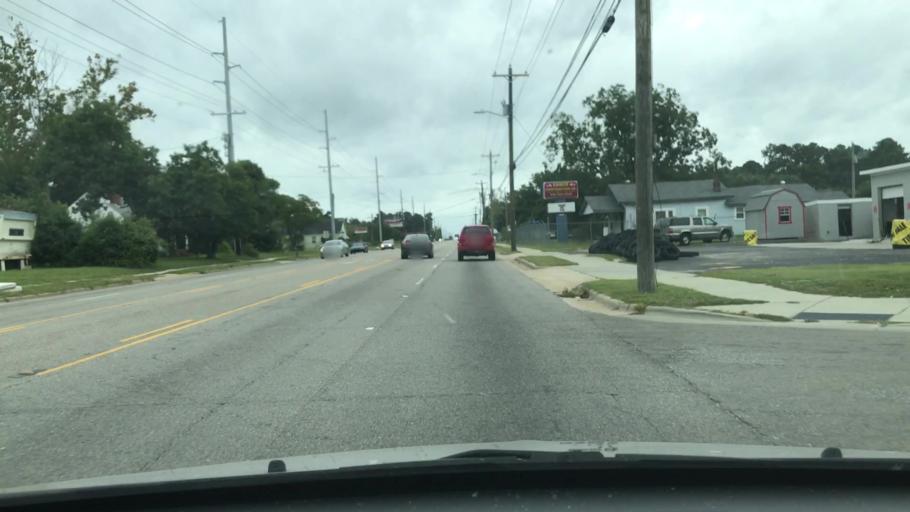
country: US
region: North Carolina
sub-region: Cumberland County
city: Fayetteville
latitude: 35.1073
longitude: -78.9243
